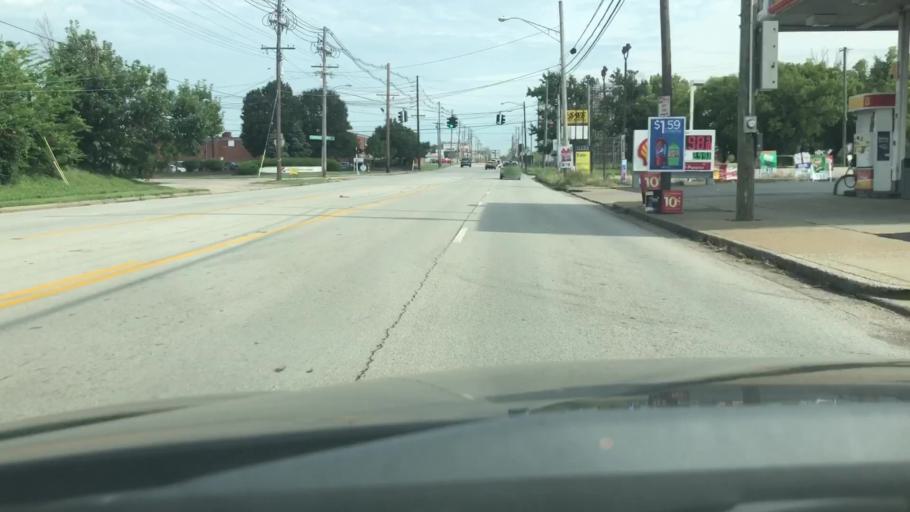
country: US
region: Kentucky
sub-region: Jefferson County
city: Audubon Park
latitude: 38.1932
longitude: -85.7509
